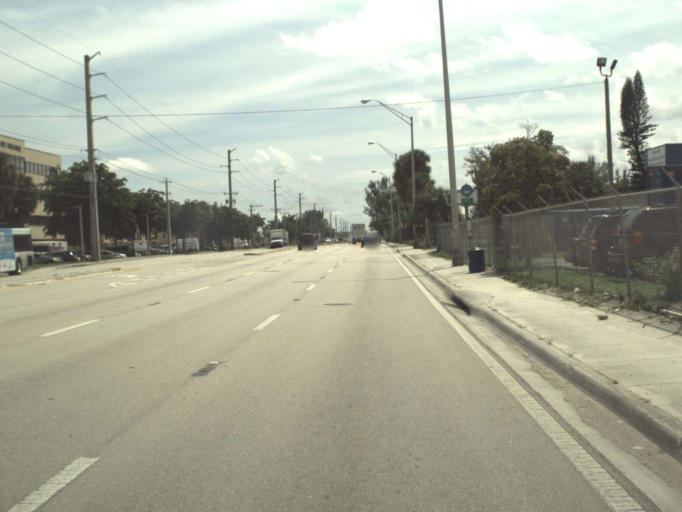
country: US
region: Florida
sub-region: Miami-Dade County
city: Virginia Gardens
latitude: 25.8195
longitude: -80.3137
